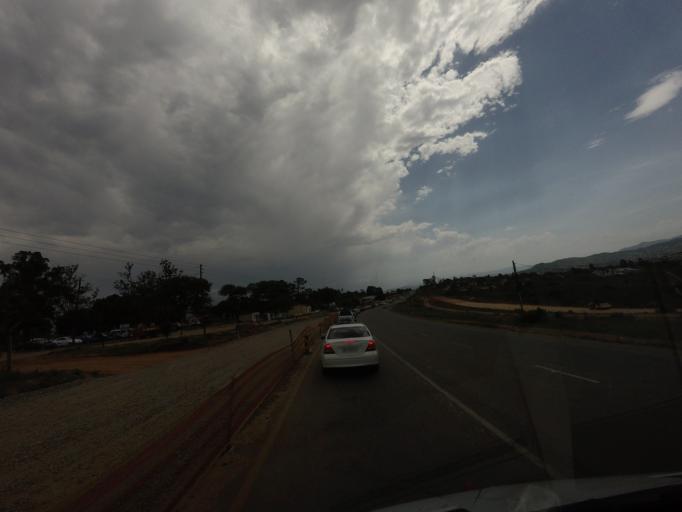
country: SZ
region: Manzini
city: Manzini
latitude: -26.4916
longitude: 31.4109
